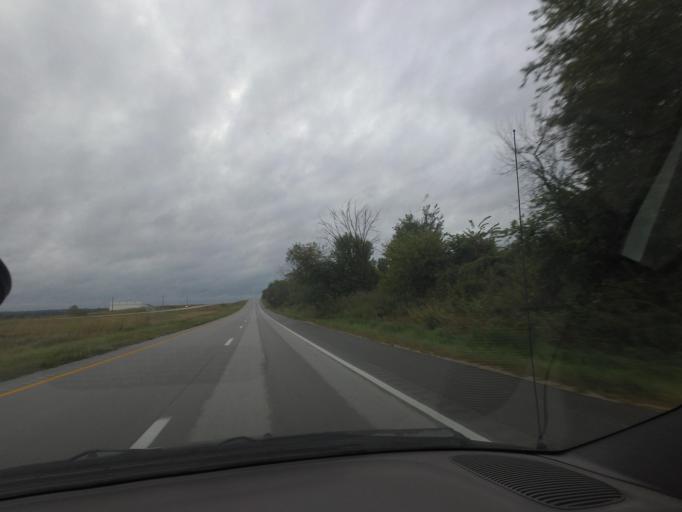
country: US
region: Missouri
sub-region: Shelby County
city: Shelbina
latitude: 39.6690
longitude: -91.9346
